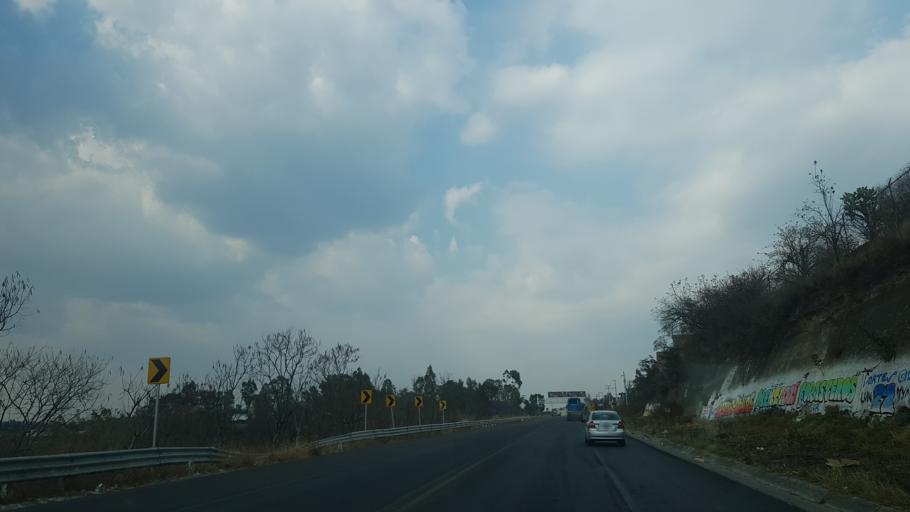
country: MX
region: Puebla
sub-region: Santa Isabel Cholula
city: Santa Ana Acozautla
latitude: 18.9539
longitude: -98.3891
